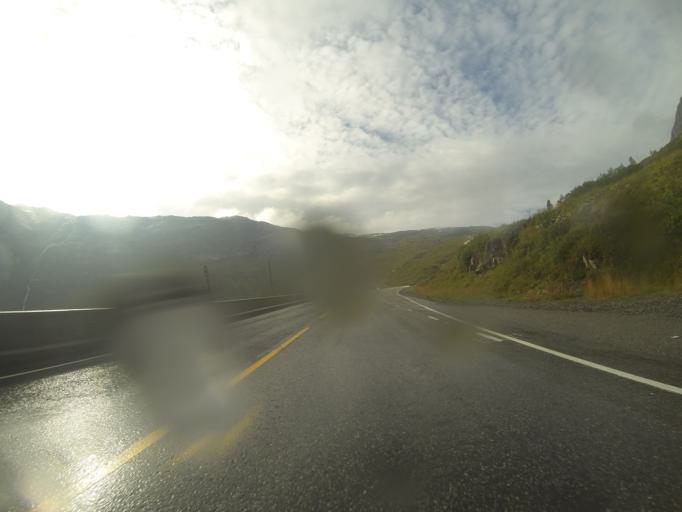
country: NO
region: Hordaland
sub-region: Odda
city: Odda
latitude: 59.8220
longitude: 6.7431
